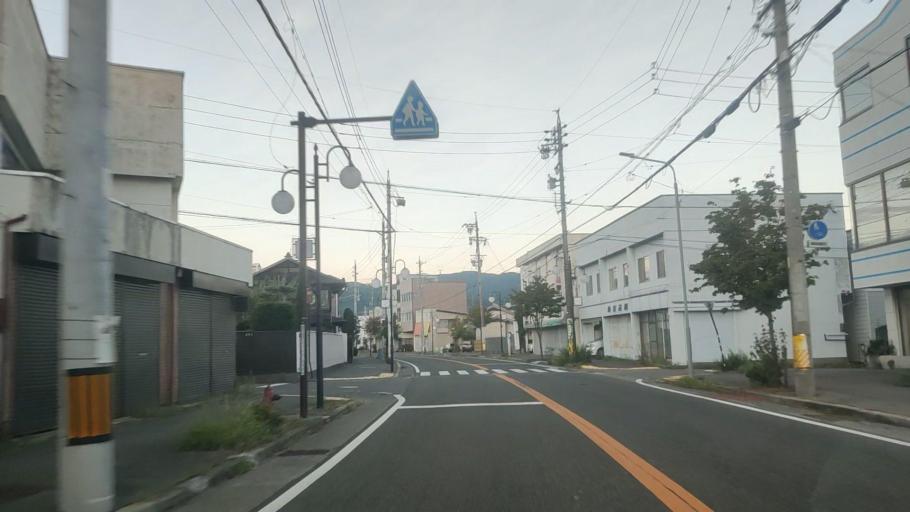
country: JP
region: Nagano
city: Okaya
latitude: 36.0694
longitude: 138.0580
